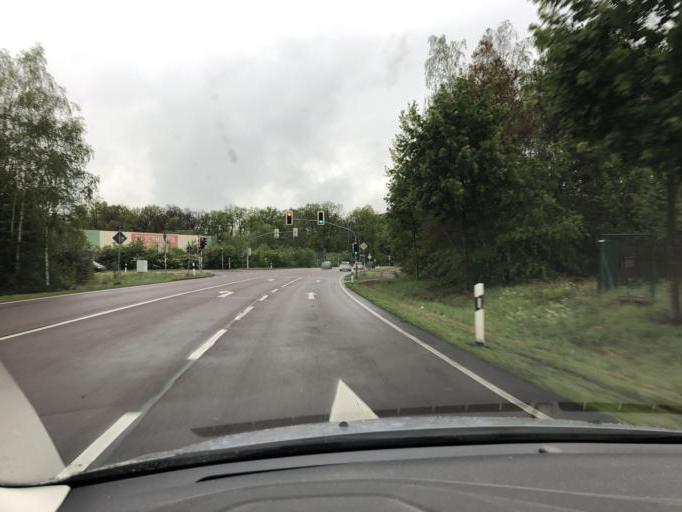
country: DE
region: Saxony-Anhalt
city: Dessau
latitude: 51.7898
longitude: 12.2358
